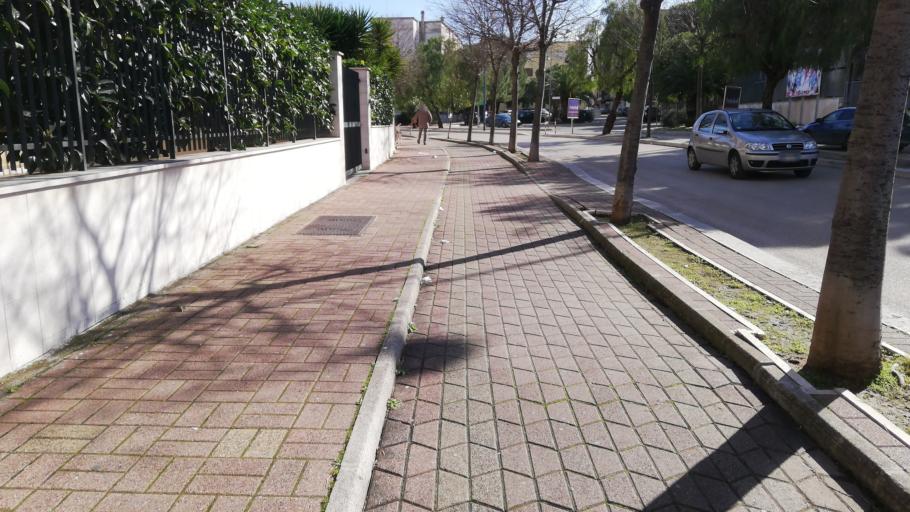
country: IT
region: Apulia
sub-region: Provincia di Barletta - Andria - Trani
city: Andria
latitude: 41.2334
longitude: 16.3021
